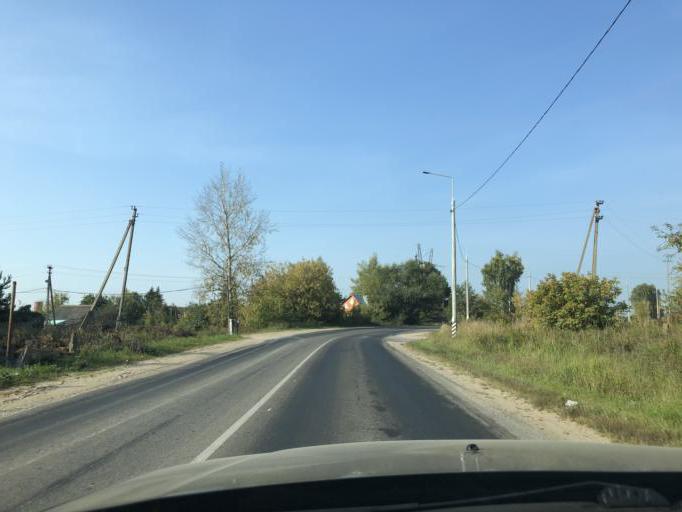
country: RU
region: Tula
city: Leninskiy
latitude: 54.2960
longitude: 37.4578
